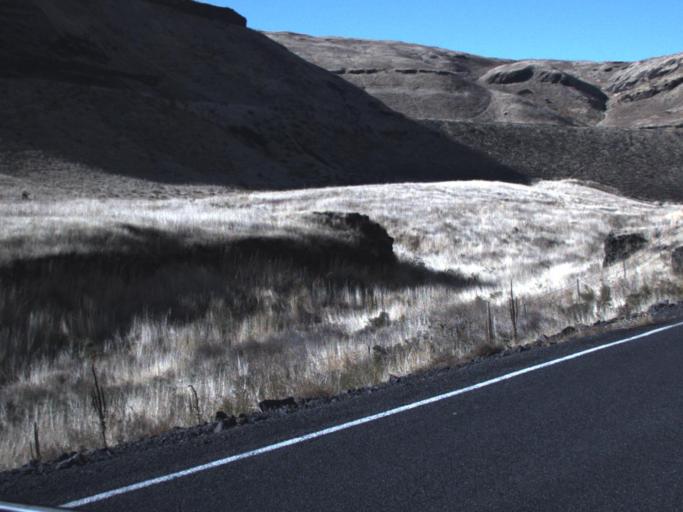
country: US
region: Washington
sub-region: Franklin County
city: Connell
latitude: 46.5831
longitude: -118.5408
